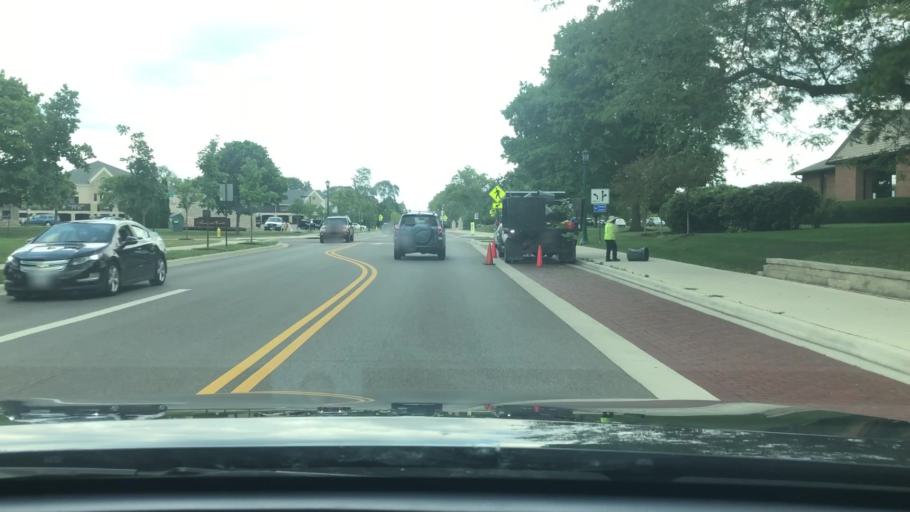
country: US
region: Ohio
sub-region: Franklin County
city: Upper Arlington
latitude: 40.0127
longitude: -83.0684
